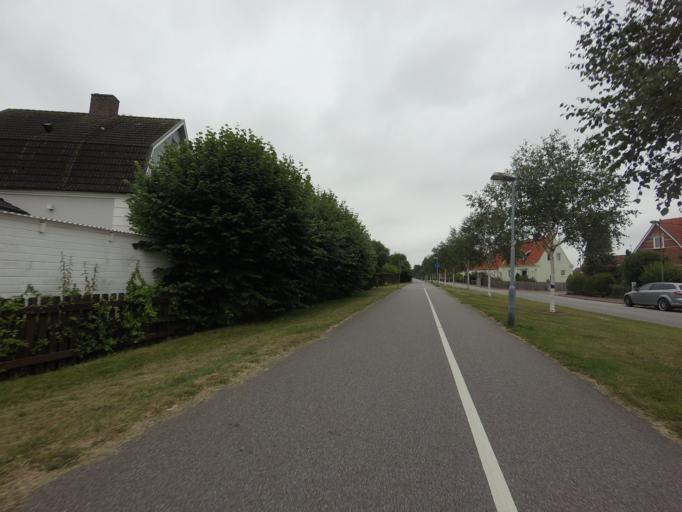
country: SE
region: Skane
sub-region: Malmo
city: Malmoe
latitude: 55.5723
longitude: 12.9973
